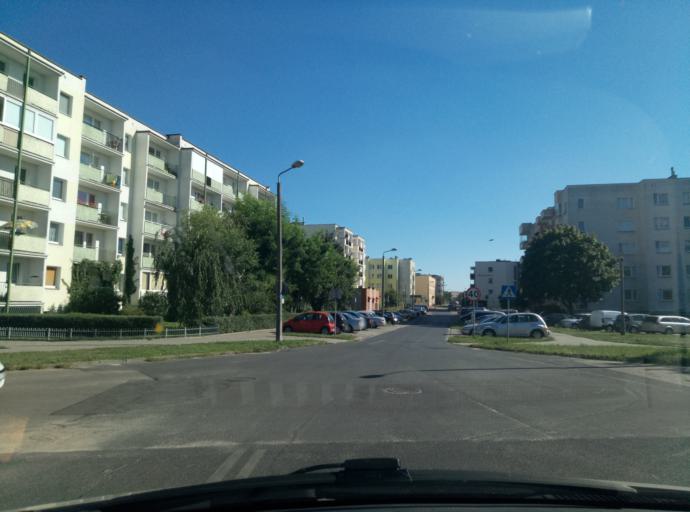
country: PL
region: Kujawsko-Pomorskie
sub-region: Torun
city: Torun
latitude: 53.0250
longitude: 18.5963
